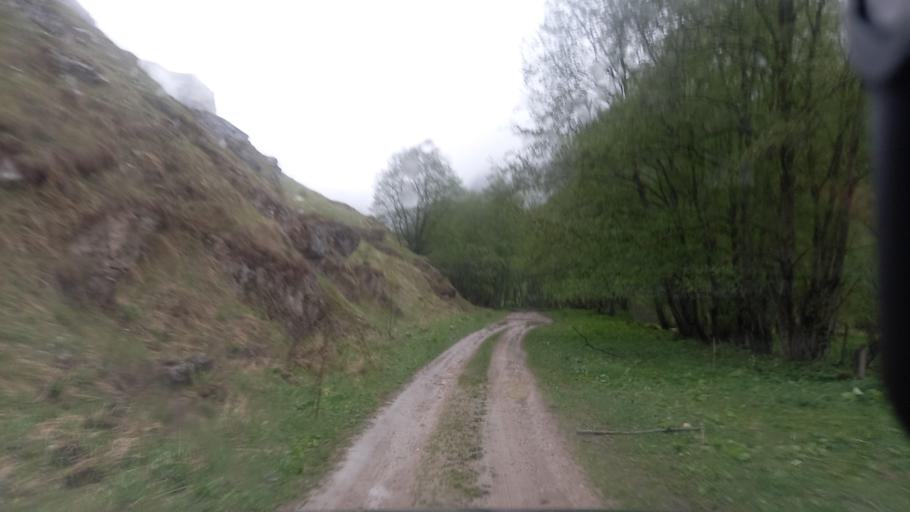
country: RU
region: Kabardino-Balkariya
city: Bylym
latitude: 43.5960
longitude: 42.9600
